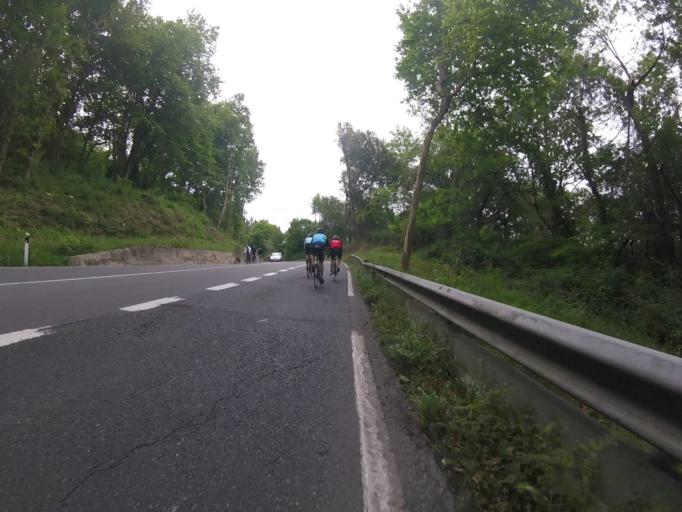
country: ES
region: Basque Country
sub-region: Provincia de Guipuzcoa
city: Orio
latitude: 43.2783
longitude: -2.1418
